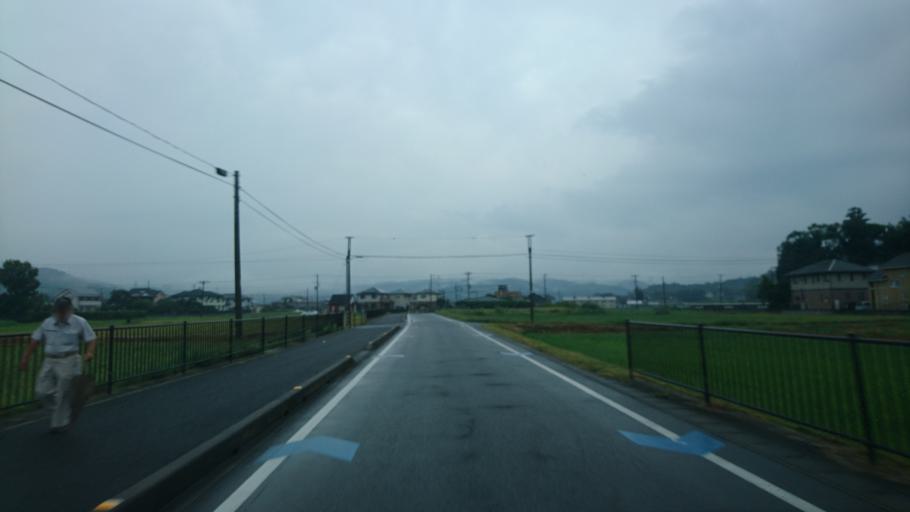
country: JP
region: Chiba
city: Kimitsu
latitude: 35.3034
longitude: 139.9654
